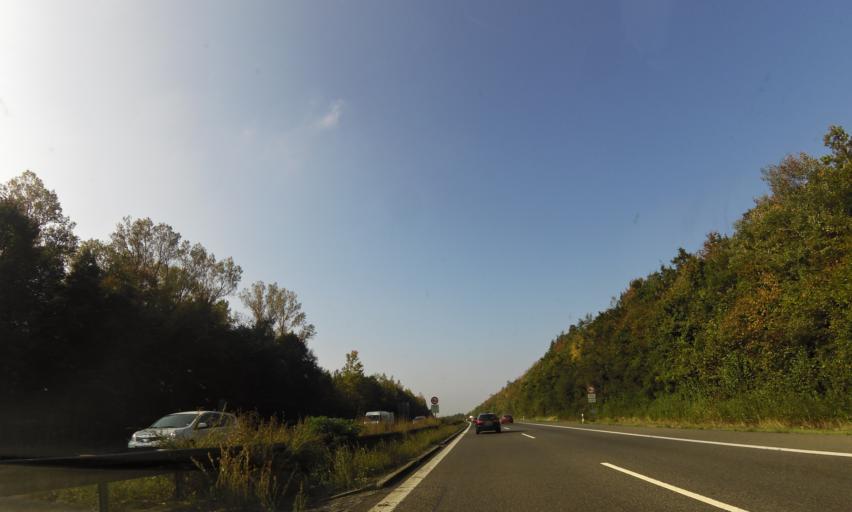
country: DE
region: Bavaria
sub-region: Regierungsbezirk Mittelfranken
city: Dombuhl
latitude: 49.2252
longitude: 10.2726
